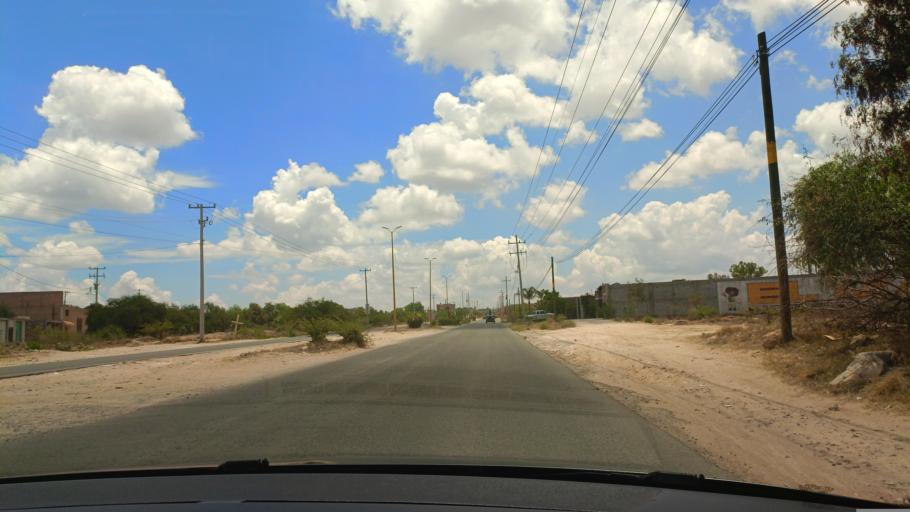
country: MX
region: Guanajuato
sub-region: San Luis de la Paz
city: San Ignacio
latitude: 21.2875
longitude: -100.5359
